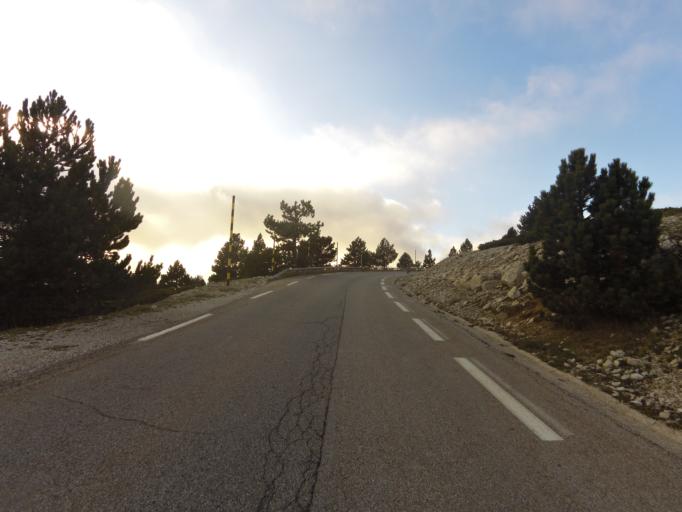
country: FR
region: Provence-Alpes-Cote d'Azur
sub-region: Departement du Vaucluse
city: Sault
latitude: 44.1549
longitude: 5.3131
